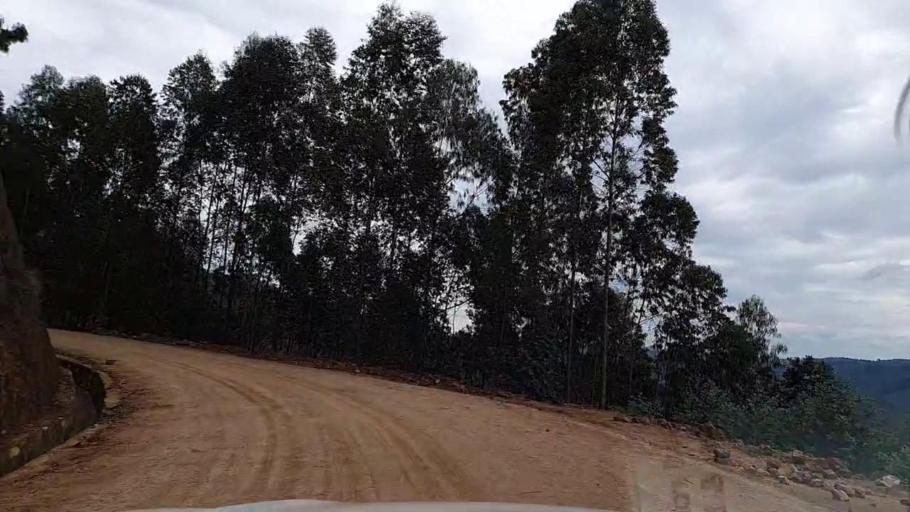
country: RW
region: Southern Province
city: Nzega
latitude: -2.3834
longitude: 29.4492
